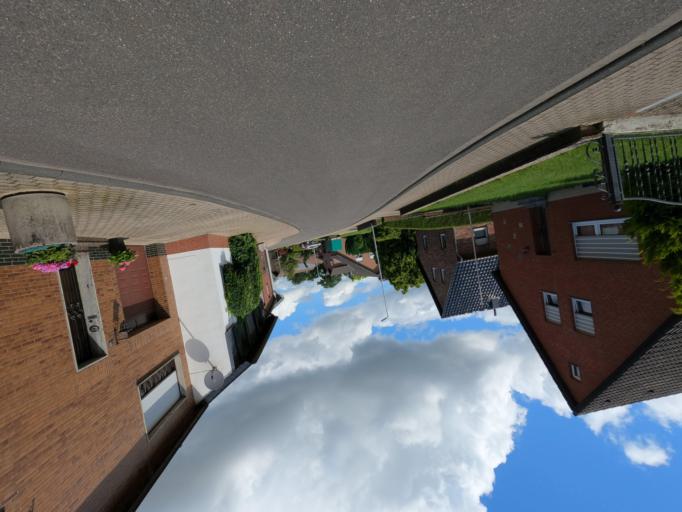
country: DE
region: North Rhine-Westphalia
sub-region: Regierungsbezirk Koln
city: Linnich
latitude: 50.9588
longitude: 6.2187
